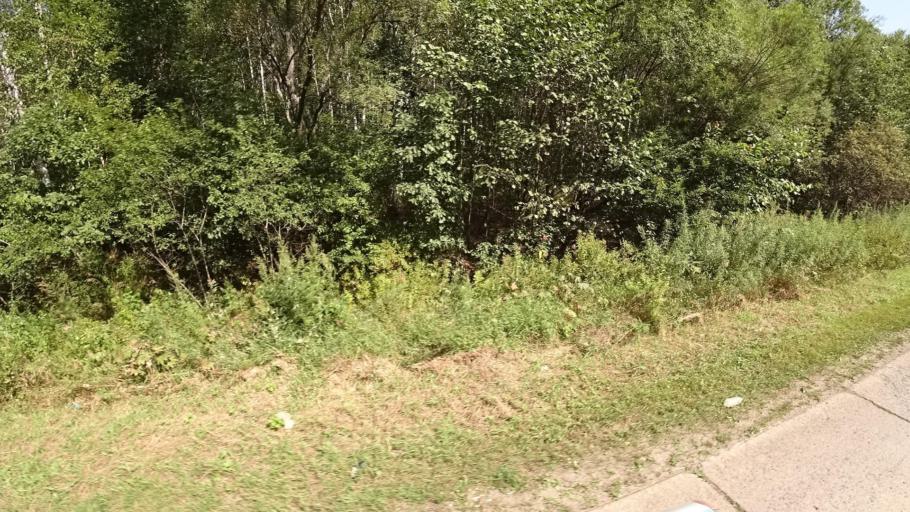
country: RU
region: Khabarovsk Krai
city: Khor
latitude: 47.9857
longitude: 135.0965
